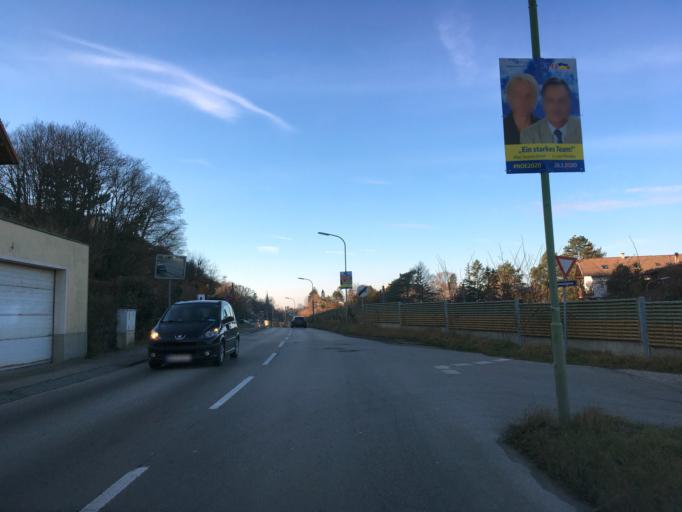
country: AT
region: Lower Austria
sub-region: Politischer Bezirk Korneuburg
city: Leobendorf
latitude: 48.3480
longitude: 16.2839
